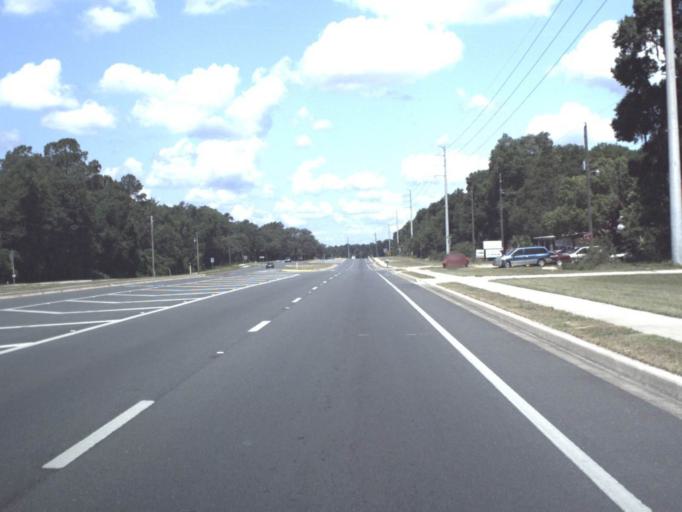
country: US
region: Florida
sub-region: Putnam County
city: Interlachen
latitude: 29.6280
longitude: -81.8674
